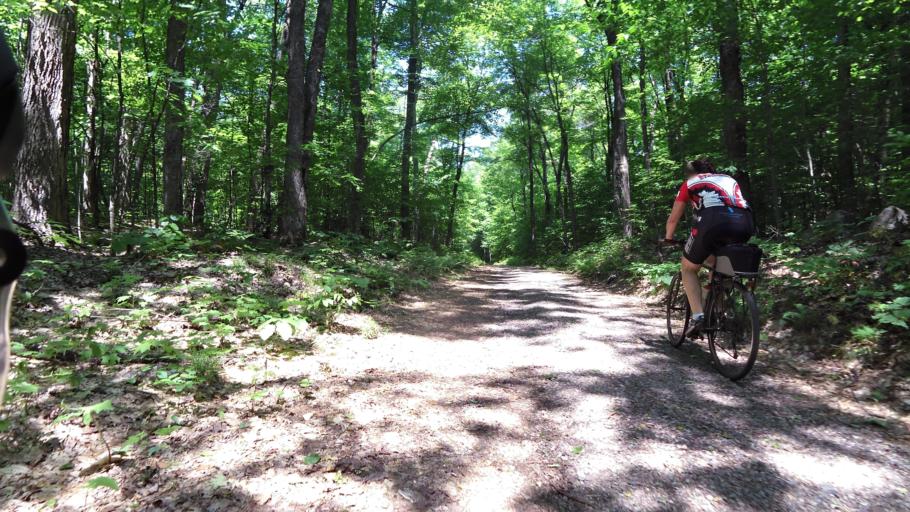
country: CA
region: Quebec
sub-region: Outaouais
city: Wakefield
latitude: 45.5748
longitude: -75.9438
